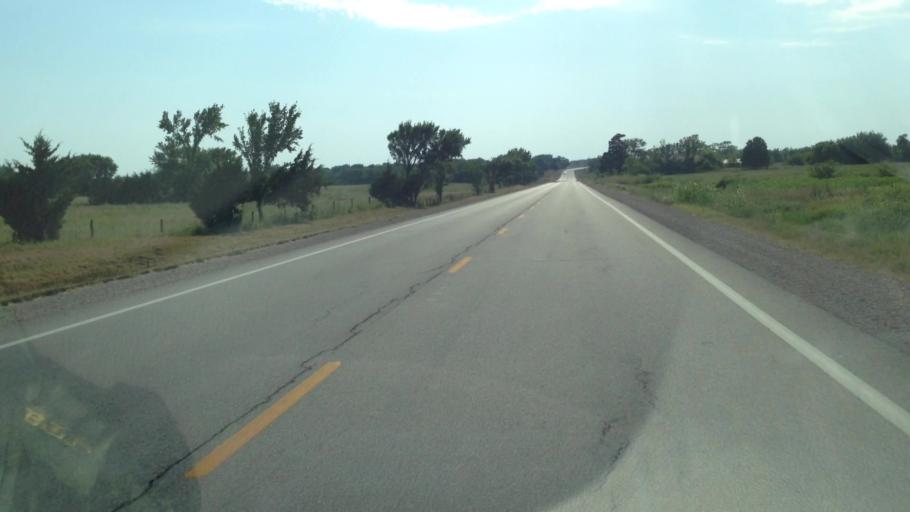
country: US
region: Kansas
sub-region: Anderson County
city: Garnett
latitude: 38.0817
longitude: -95.2283
